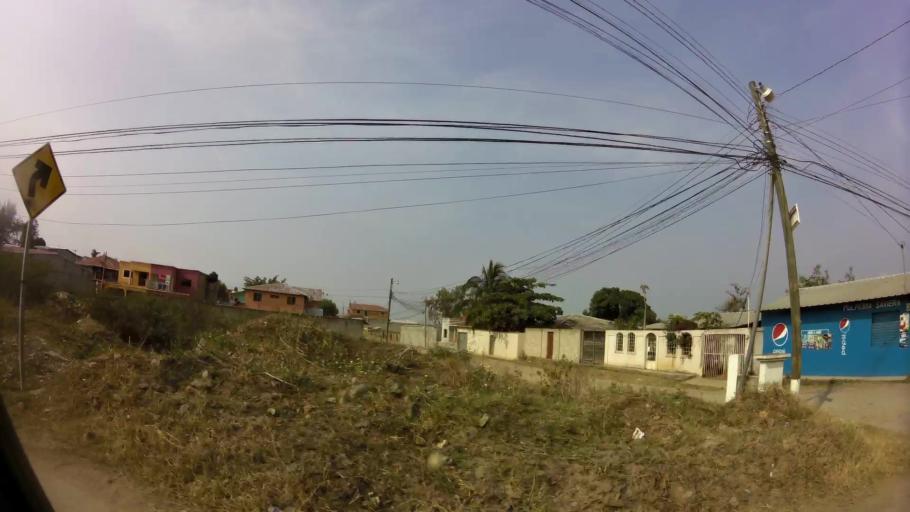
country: HN
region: Comayagua
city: Comayagua
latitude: 14.4508
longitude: -87.6190
